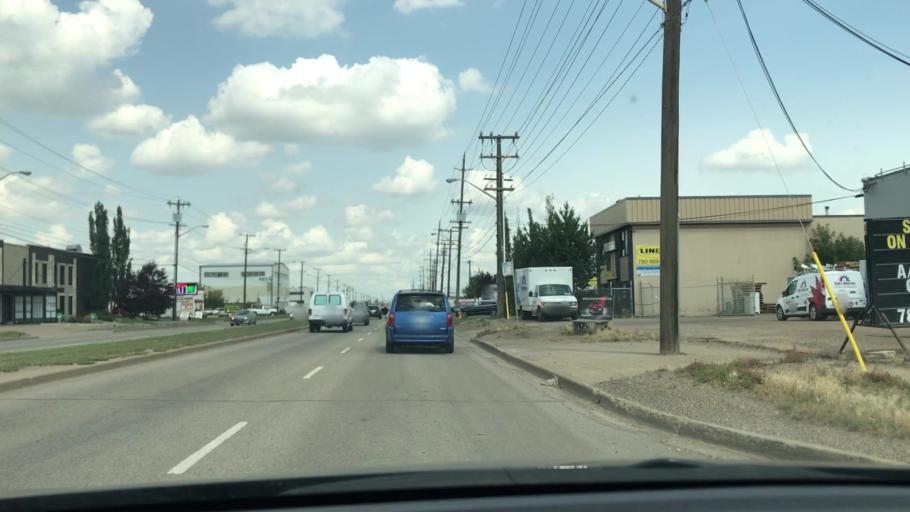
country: CA
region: Alberta
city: Edmonton
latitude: 53.5083
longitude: -113.4182
